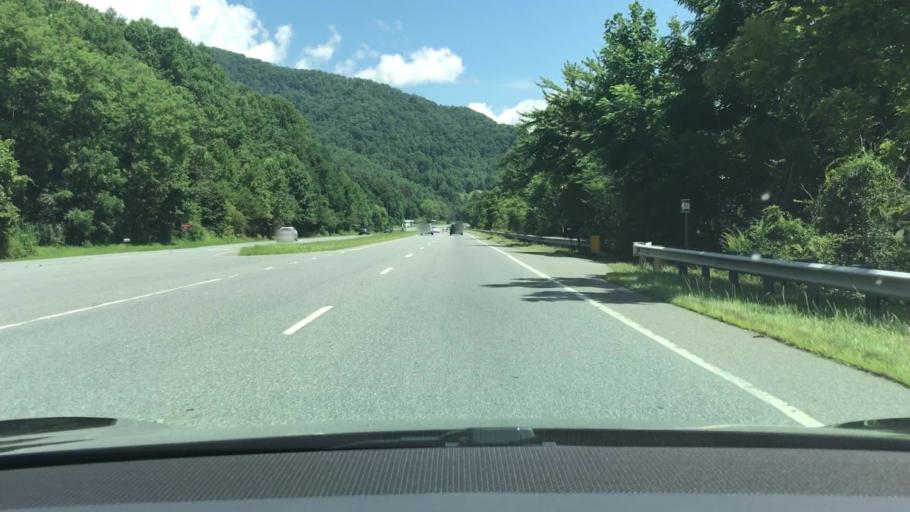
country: US
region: North Carolina
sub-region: Jackson County
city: Sylva
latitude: 35.2844
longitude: -83.2849
